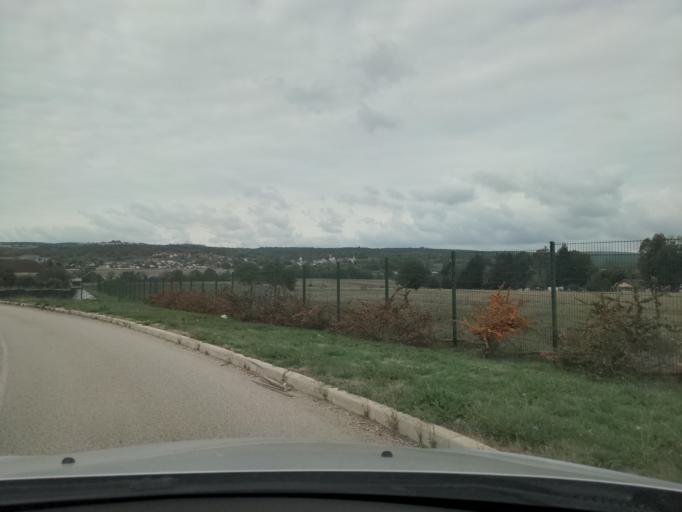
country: FR
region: Bourgogne
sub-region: Departement de la Cote-d'Or
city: Ahuy
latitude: 47.3661
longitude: 5.0393
